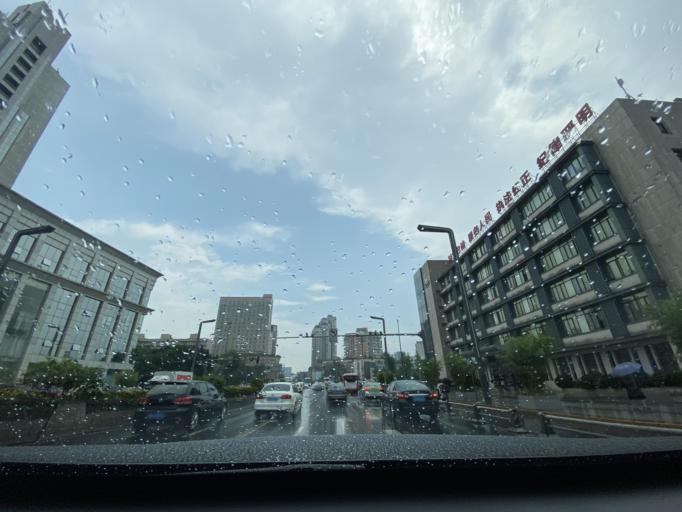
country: CN
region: Sichuan
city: Chengdu
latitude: 30.6496
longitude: 104.0725
